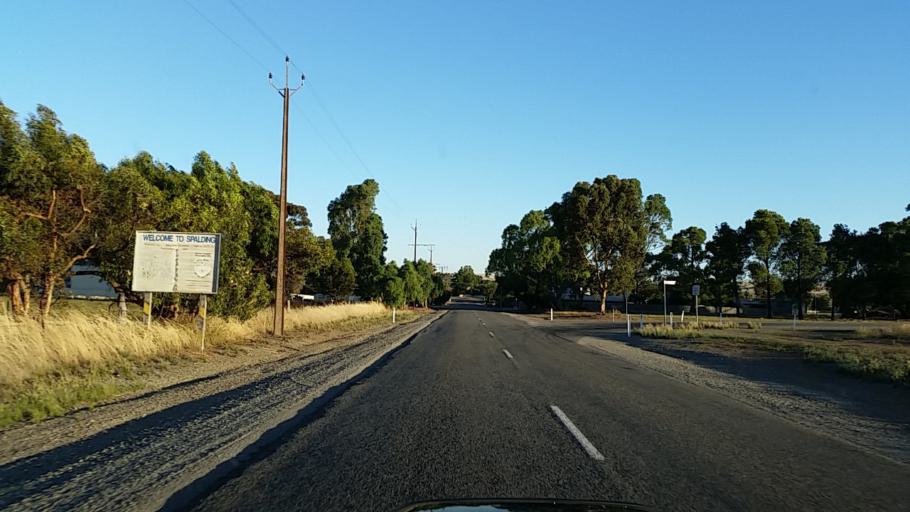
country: AU
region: South Australia
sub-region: Northern Areas
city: Jamestown
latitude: -33.4967
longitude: 138.6051
